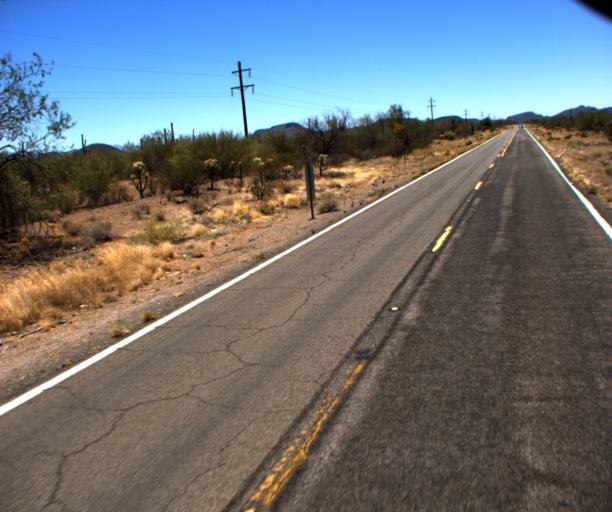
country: US
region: Arizona
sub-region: Pima County
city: Sells
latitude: 32.0183
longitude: -112.0000
